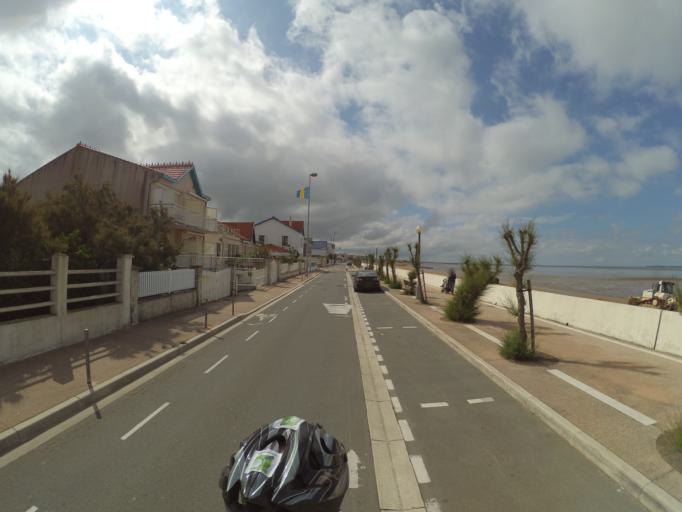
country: FR
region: Poitou-Charentes
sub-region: Departement de la Charente-Maritime
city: Chatelaillon-Plage
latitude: 46.0816
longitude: -1.0960
